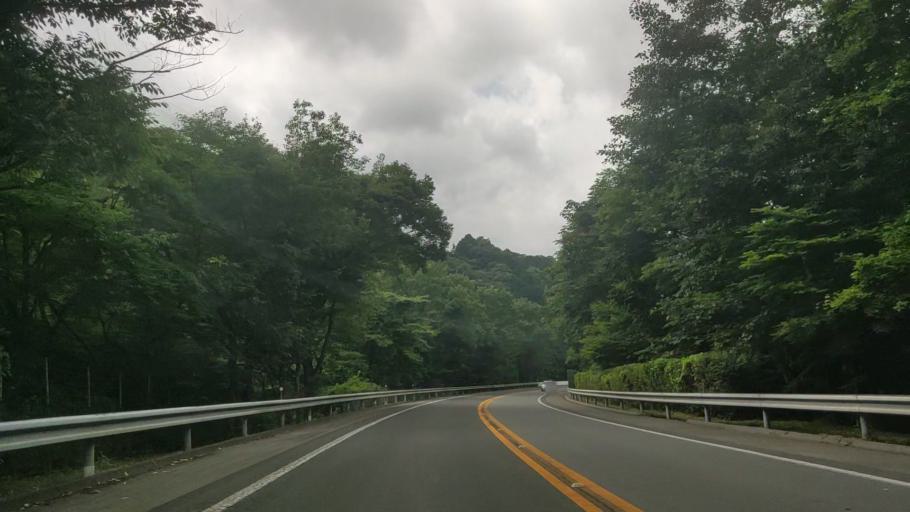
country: JP
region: Tochigi
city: Nikko
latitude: 36.7470
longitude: 139.5808
